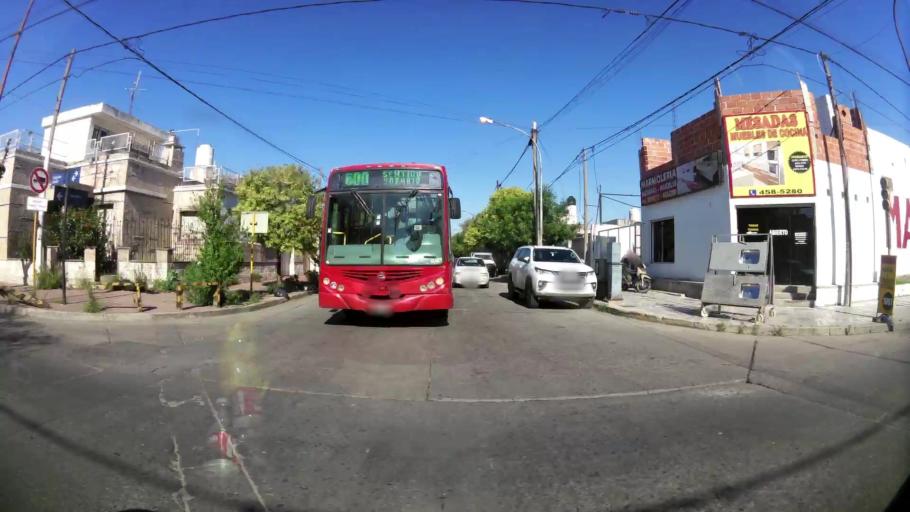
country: AR
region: Cordoba
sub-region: Departamento de Capital
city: Cordoba
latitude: -31.4199
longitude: -64.1502
